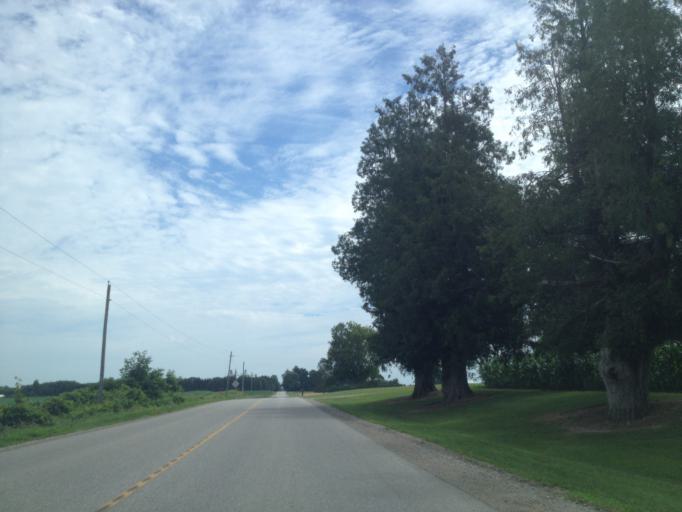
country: CA
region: Ontario
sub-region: Oxford County
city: Woodstock
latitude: 42.9952
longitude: -80.6450
